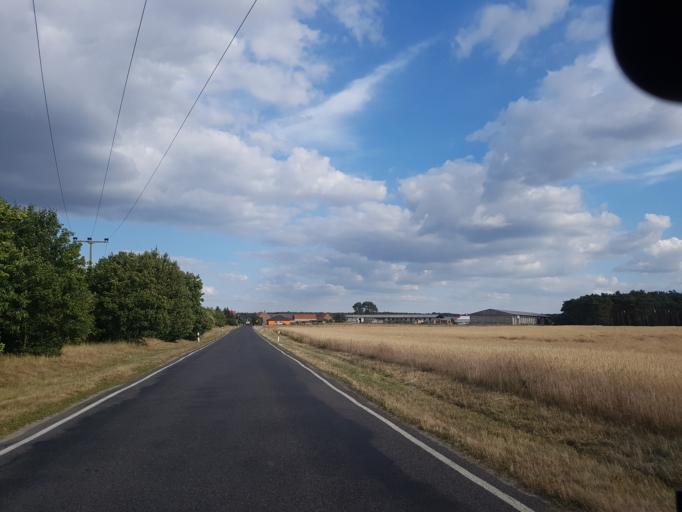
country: DE
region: Brandenburg
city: Herzberg
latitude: 51.7523
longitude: 13.2739
